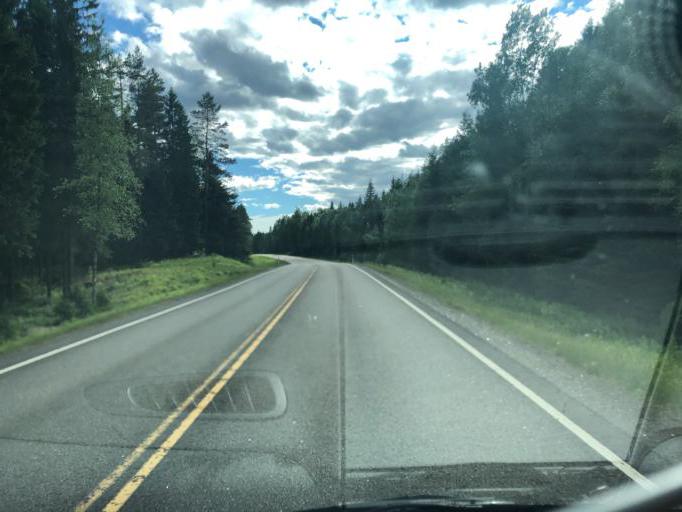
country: FI
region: Kymenlaakso
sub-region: Kouvola
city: Kouvola
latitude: 60.9988
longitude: 26.9311
